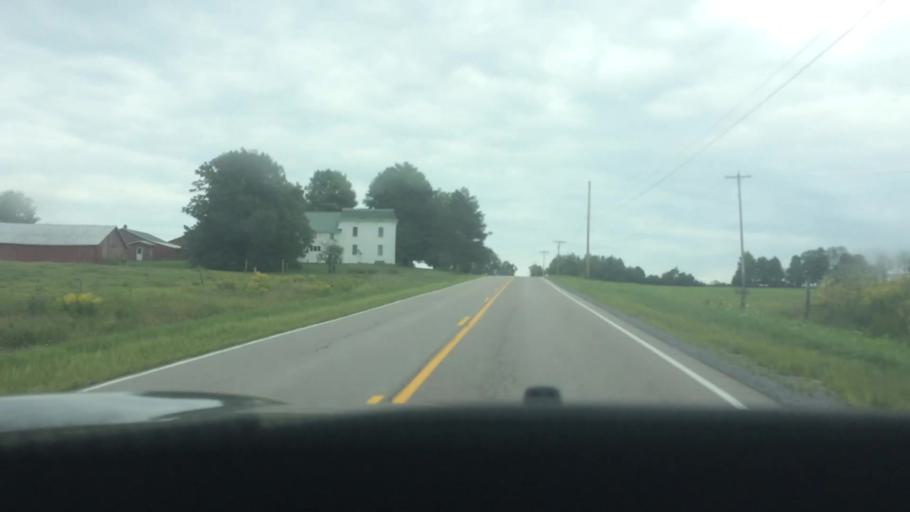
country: US
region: New York
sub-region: St. Lawrence County
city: Hannawa Falls
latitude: 44.5379
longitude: -75.0430
